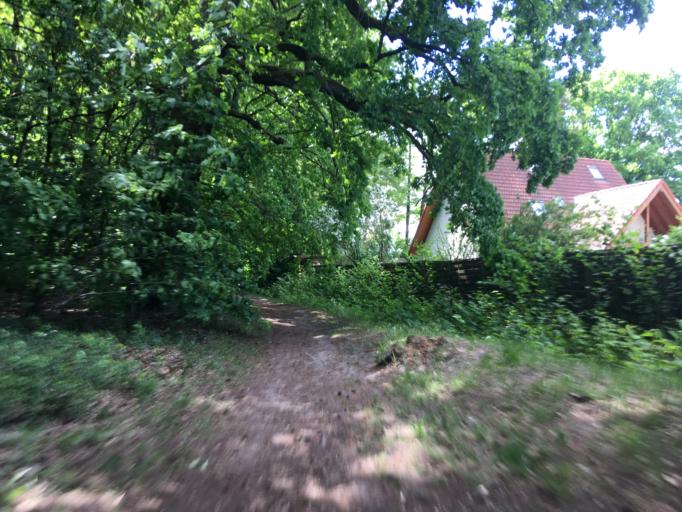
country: DE
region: Berlin
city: Bohnsdorf
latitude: 52.4024
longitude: 13.5834
